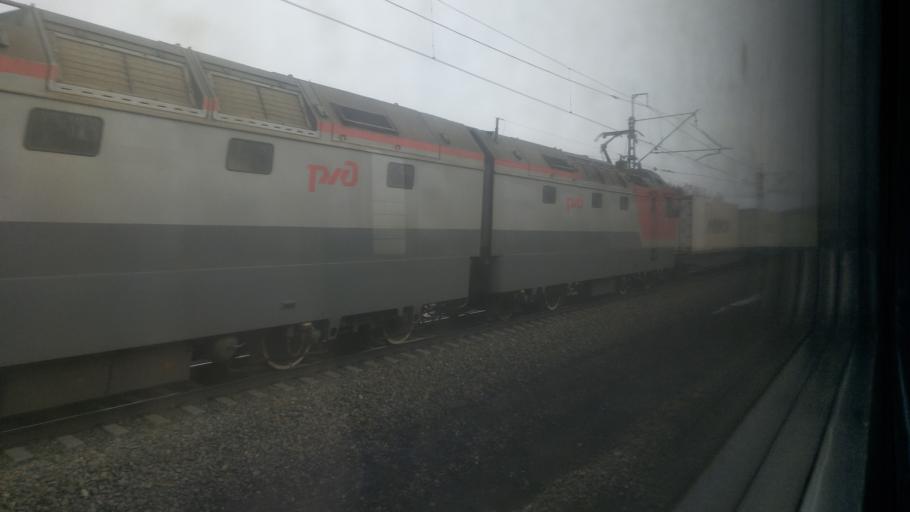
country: RU
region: Novosibirsk
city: Stantsionno-Oyashinskiy
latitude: 55.5116
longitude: 83.9400
